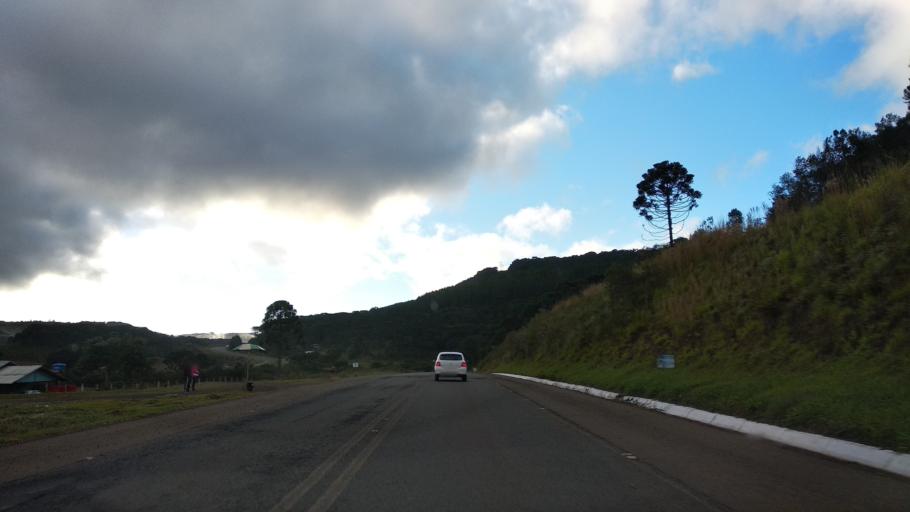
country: BR
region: Santa Catarina
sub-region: Curitibanos
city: Curitibanos
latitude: -27.5778
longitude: -50.7763
